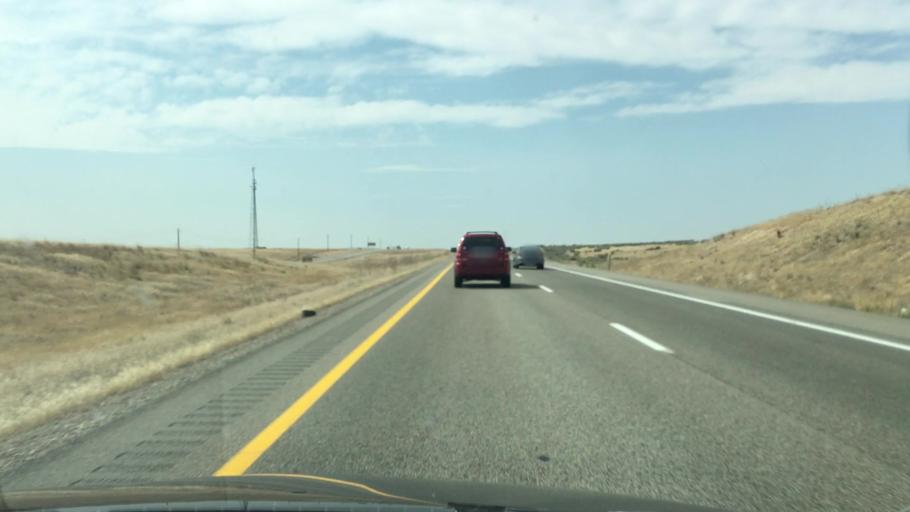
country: US
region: Idaho
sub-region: Ada County
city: Boise
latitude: 43.4467
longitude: -116.0739
